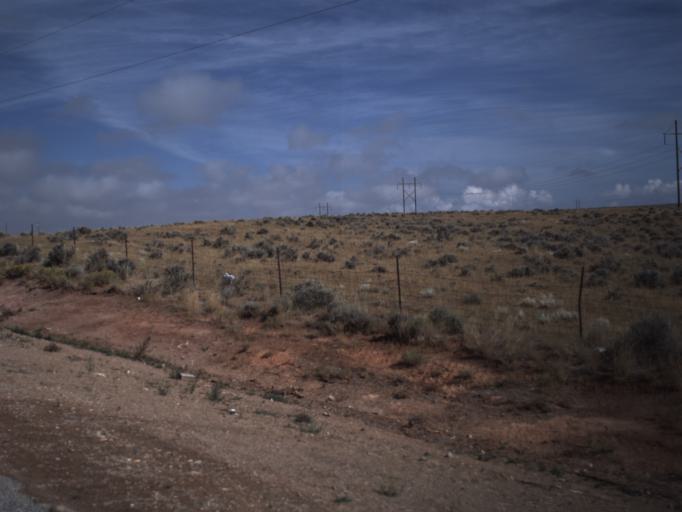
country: US
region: Wyoming
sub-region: Uinta County
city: Evanston
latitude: 41.4203
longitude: -111.0501
